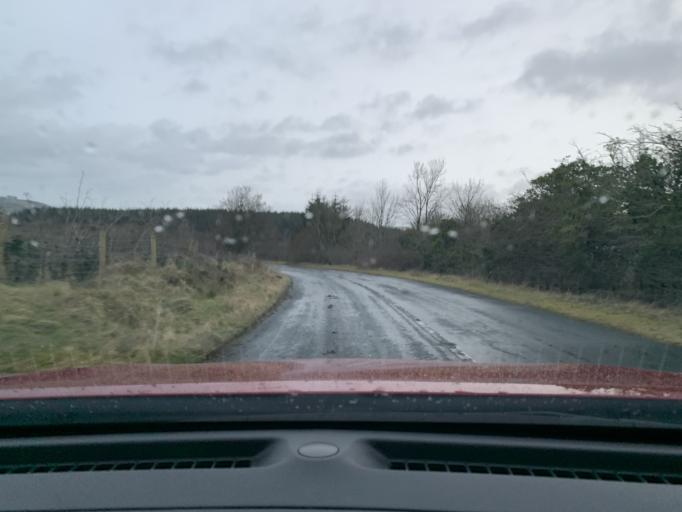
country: IE
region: Connaught
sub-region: Roscommon
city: Boyle
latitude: 54.0168
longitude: -8.3243
